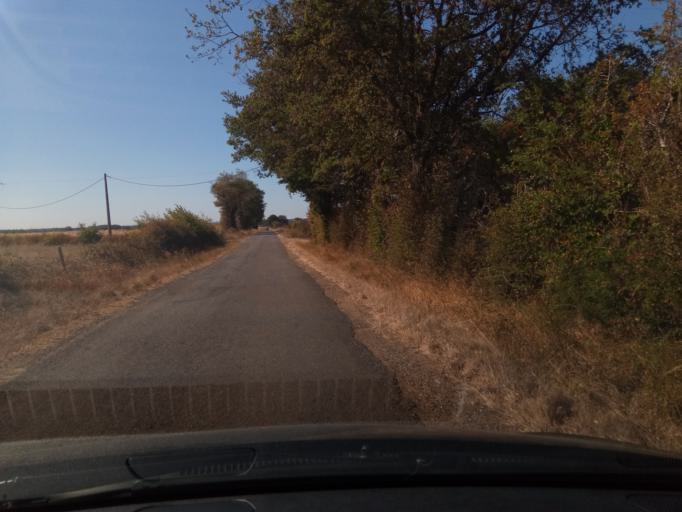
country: FR
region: Poitou-Charentes
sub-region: Departement de la Vienne
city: Montmorillon
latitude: 46.4815
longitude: 0.8813
